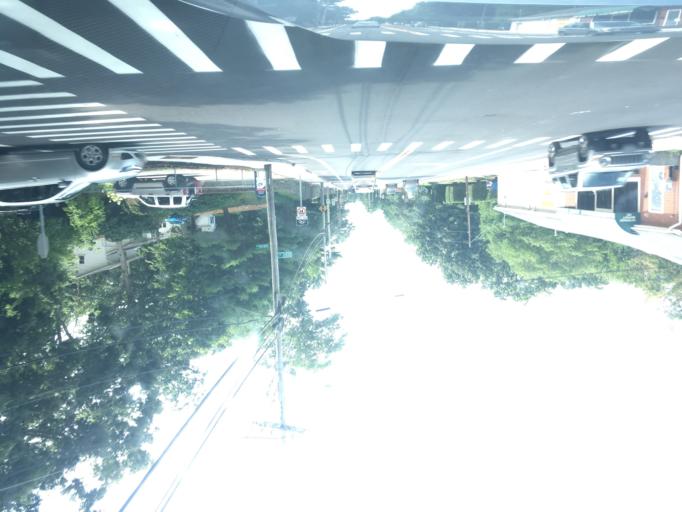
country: US
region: Rhode Island
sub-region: Kent County
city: West Warwick
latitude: 41.6764
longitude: -71.5559
